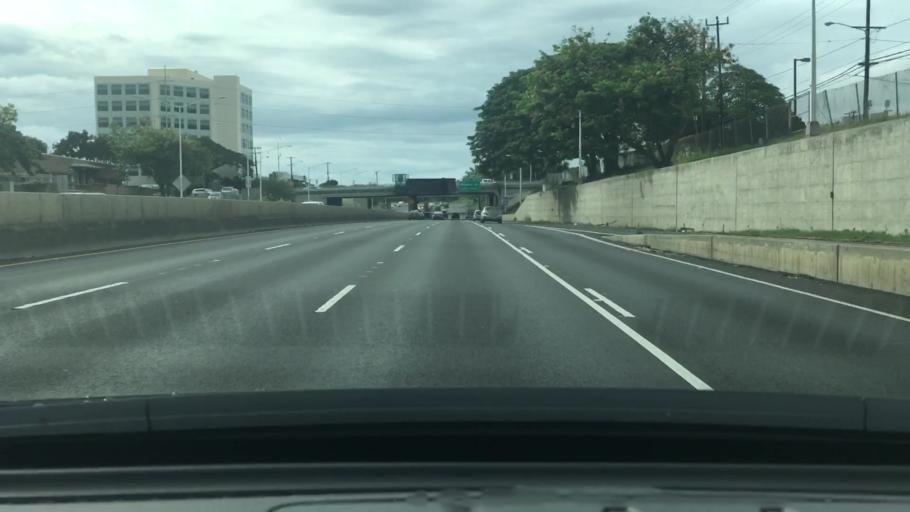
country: US
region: Hawaii
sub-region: Honolulu County
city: Honolulu
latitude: 21.3202
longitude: -157.8591
